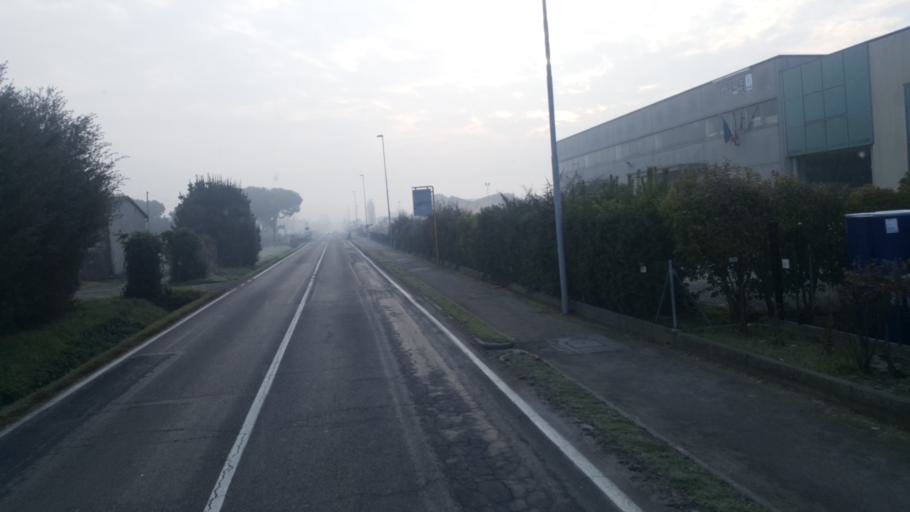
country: IT
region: Emilia-Romagna
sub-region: Provincia di Ravenna
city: Bagnacavallo
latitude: 44.4102
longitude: 11.9933
